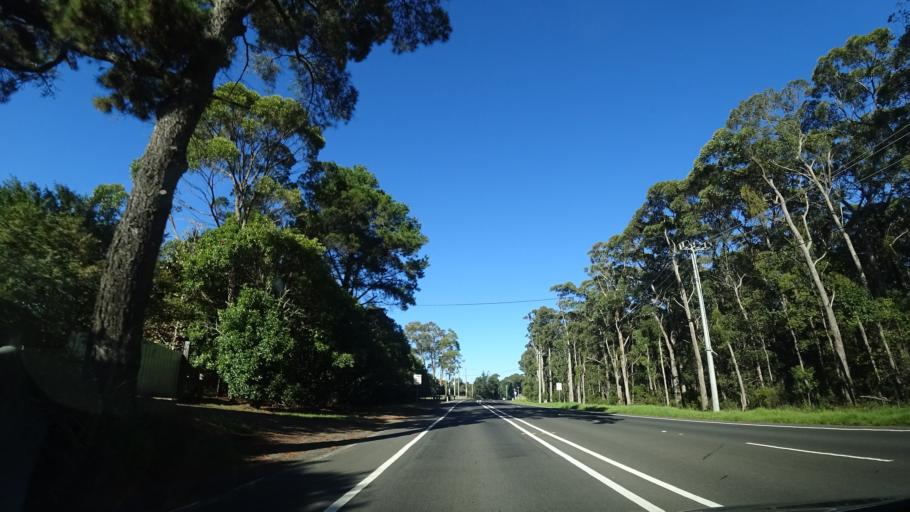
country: AU
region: New South Wales
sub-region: Blue Mountains Municipality
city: Hazelbrook
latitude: -33.5051
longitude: 150.5049
